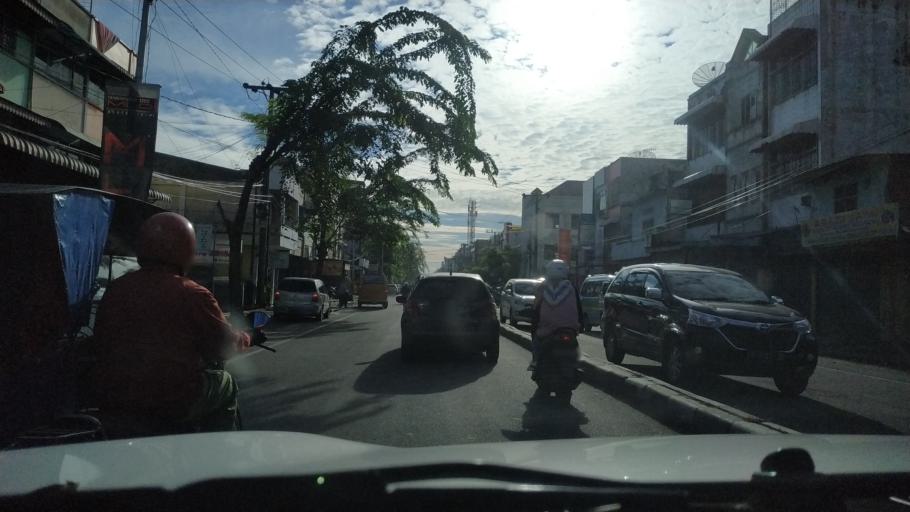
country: ID
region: North Sumatra
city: Medan
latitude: 3.5986
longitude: 98.6925
